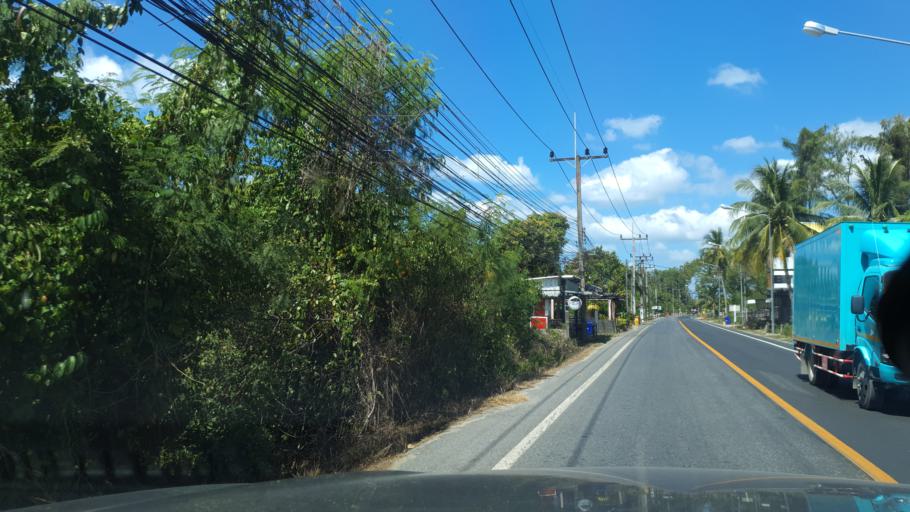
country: TH
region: Phuket
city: Thalang
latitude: 8.1369
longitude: 98.3067
